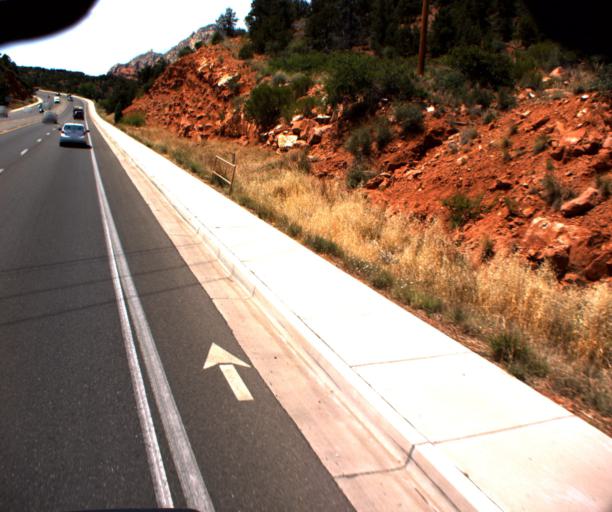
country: US
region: Arizona
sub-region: Coconino County
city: Sedona
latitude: 34.8665
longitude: -111.7665
